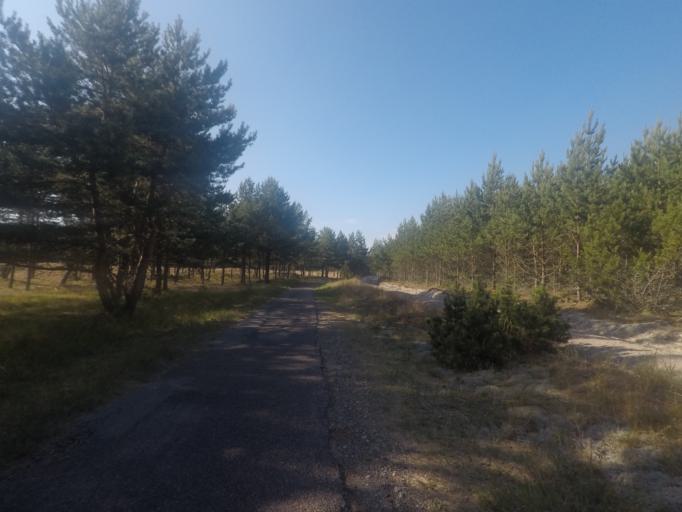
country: LT
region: Klaipedos apskritis
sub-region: Klaipeda
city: Klaipeda
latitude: 55.5731
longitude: 21.1136
